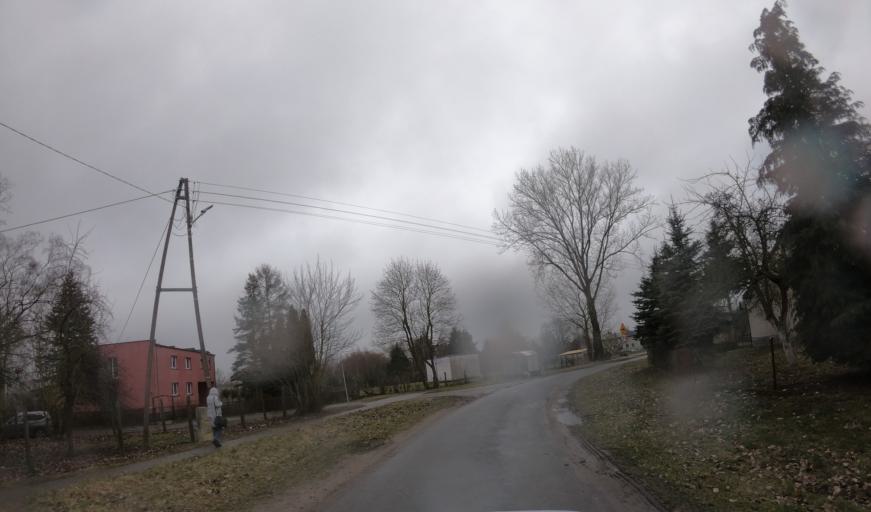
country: PL
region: West Pomeranian Voivodeship
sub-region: Powiat kamienski
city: Kamien Pomorski
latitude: 53.9016
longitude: 14.8287
